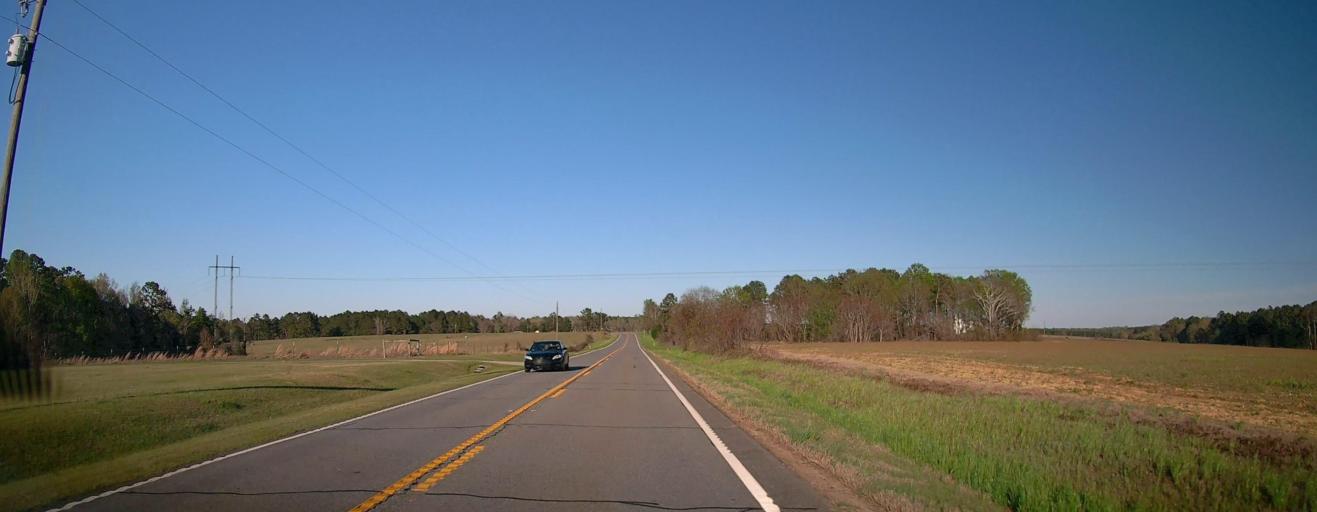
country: US
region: Georgia
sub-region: Pulaski County
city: Hawkinsville
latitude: 32.2497
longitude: -83.5815
